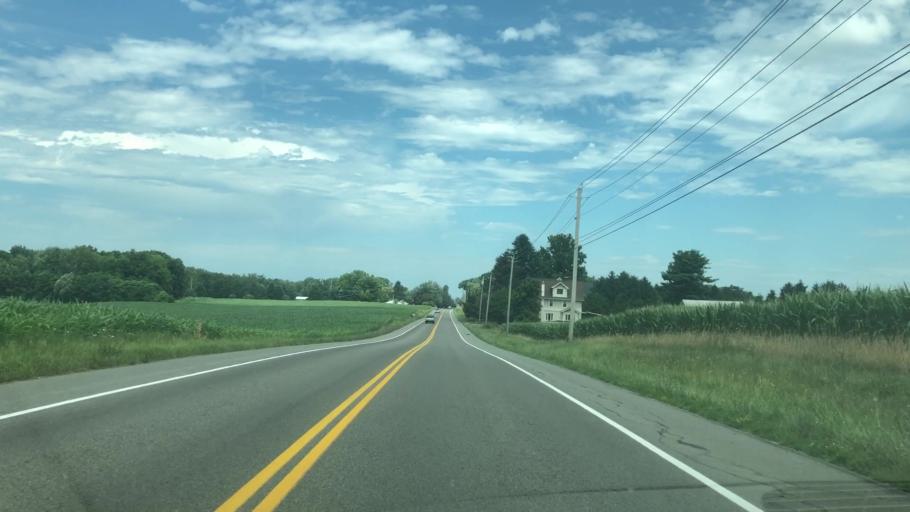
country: US
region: New York
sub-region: Monroe County
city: Webster
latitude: 43.2063
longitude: -77.4004
